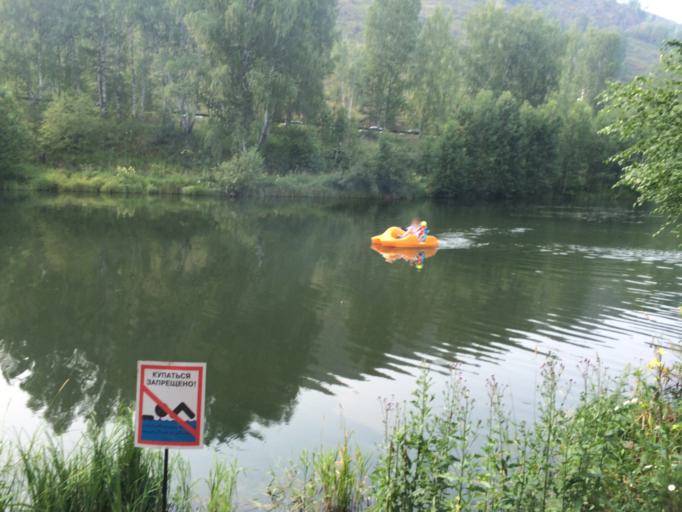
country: RU
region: Bashkortostan
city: Abzakovo
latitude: 53.7964
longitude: 58.6290
